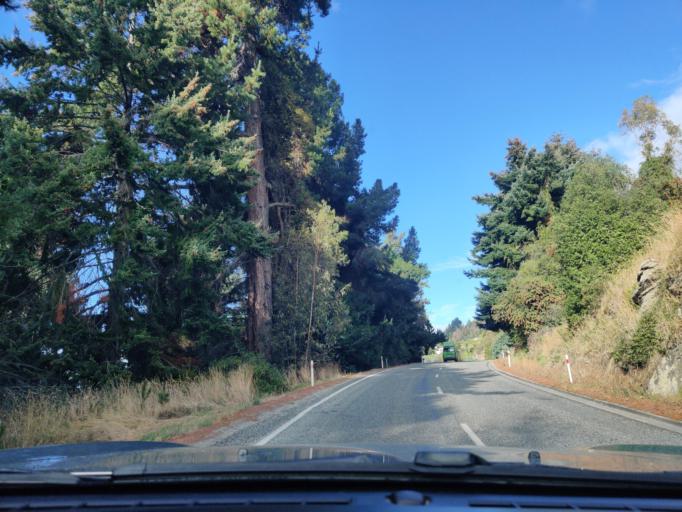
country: NZ
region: Otago
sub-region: Queenstown-Lakes District
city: Queenstown
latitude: -45.0399
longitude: 168.6398
